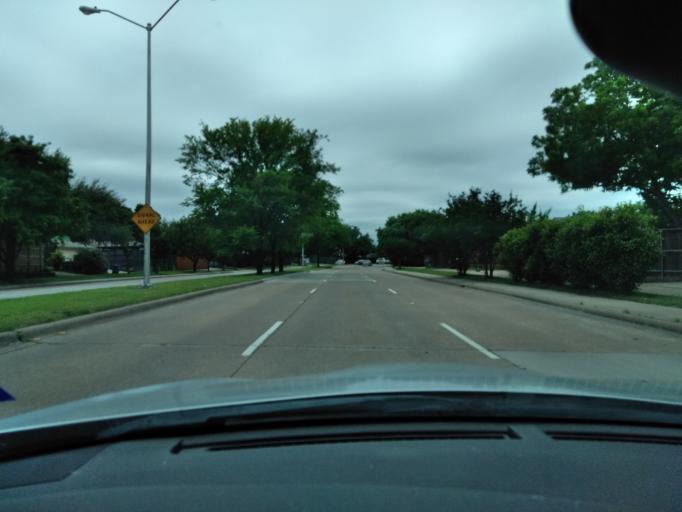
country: US
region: Texas
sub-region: Dallas County
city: Addison
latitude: 32.9722
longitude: -96.7841
